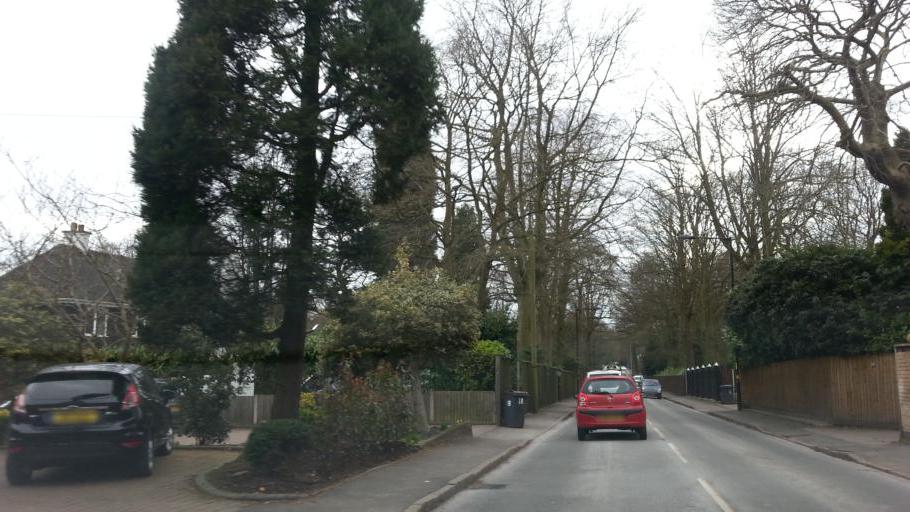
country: GB
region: England
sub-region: Walsall
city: Streetly
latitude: 52.5895
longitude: -1.8664
